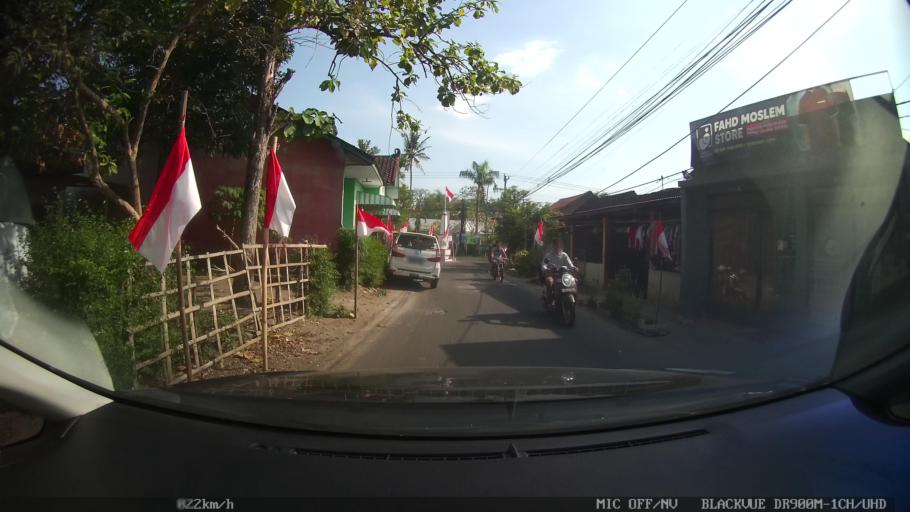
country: ID
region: Daerah Istimewa Yogyakarta
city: Kasihan
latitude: -7.8418
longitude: 110.3323
